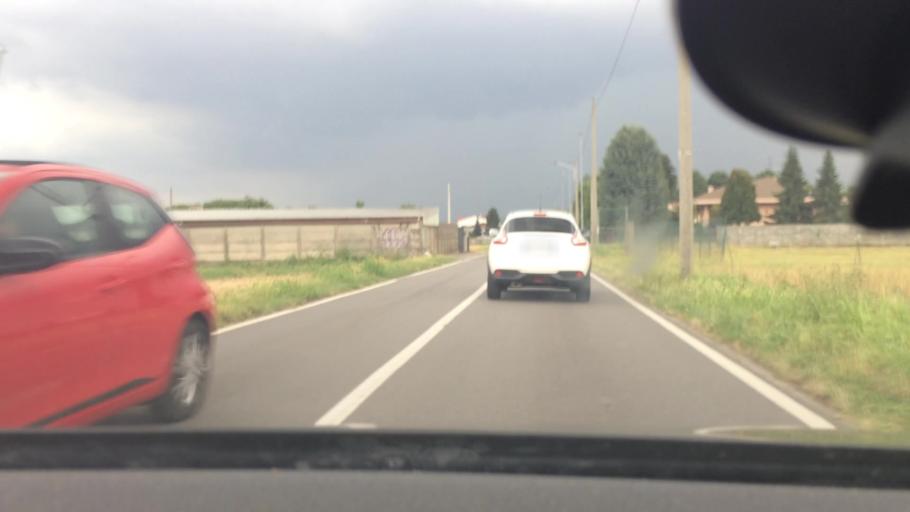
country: IT
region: Lombardy
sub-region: Citta metropolitana di Milano
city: Cantalupo
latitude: 45.5740
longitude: 8.9838
